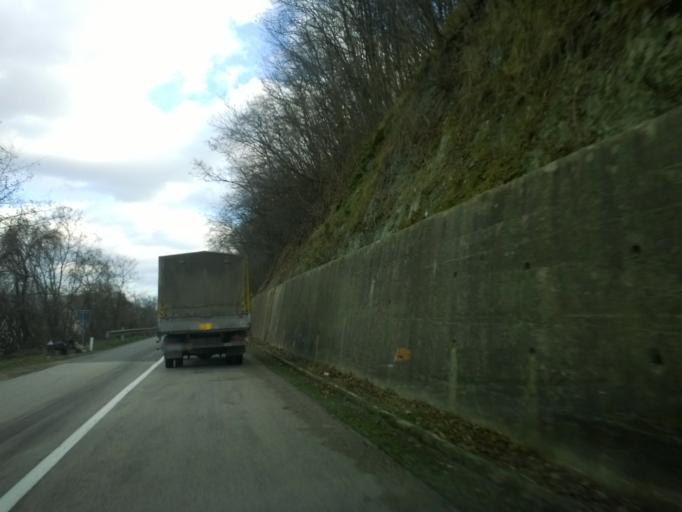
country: RO
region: Caras-Severin
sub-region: Comuna Berzasca
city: Liubcova
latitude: 44.6472
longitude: 21.8494
